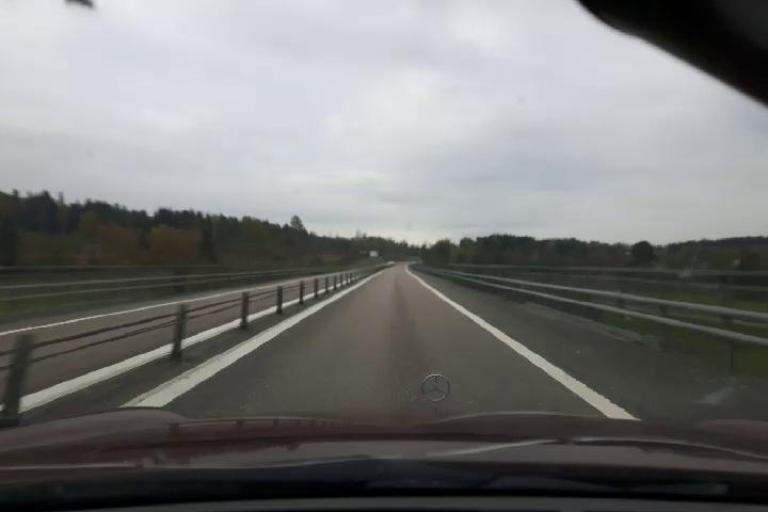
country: SE
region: Vaesternorrland
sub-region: Kramfors Kommun
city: Nordingra
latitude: 62.9216
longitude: 18.0993
